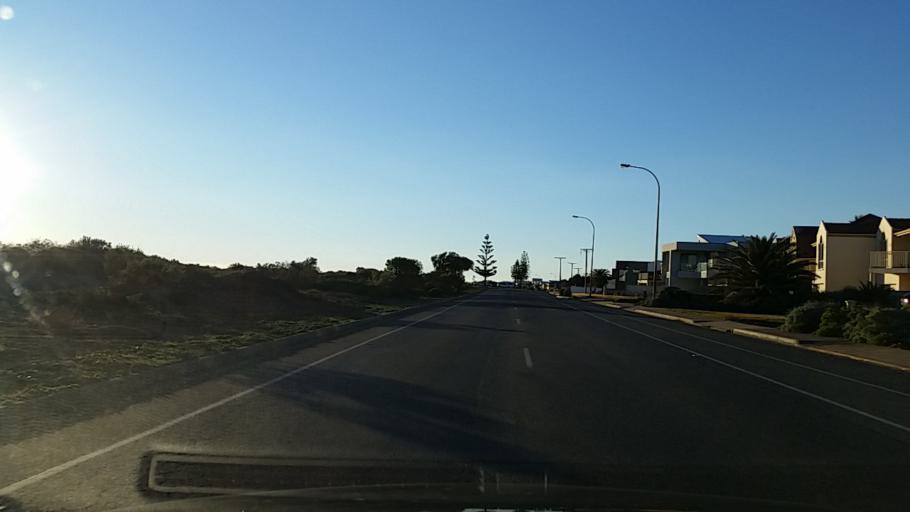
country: AU
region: South Australia
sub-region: Onkaparinga
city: Seaford
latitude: -35.1896
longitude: 138.4694
